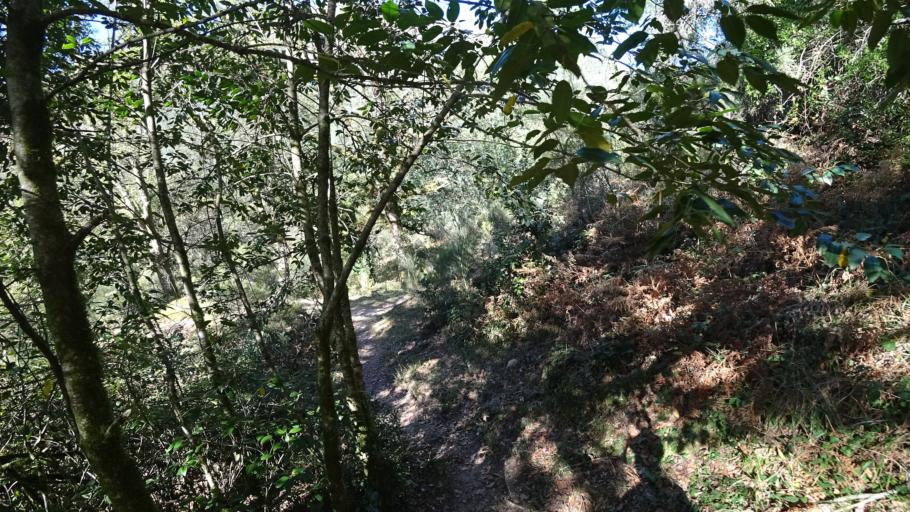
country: PT
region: Braga
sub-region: Vieira do Minho
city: Real
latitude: 41.7546
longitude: -8.1496
